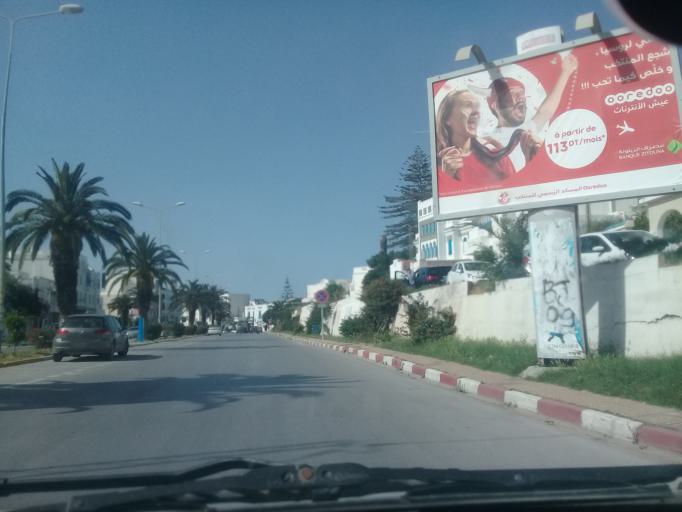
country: TN
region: Tunis
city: Al Marsa
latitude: 36.8775
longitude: 10.3269
